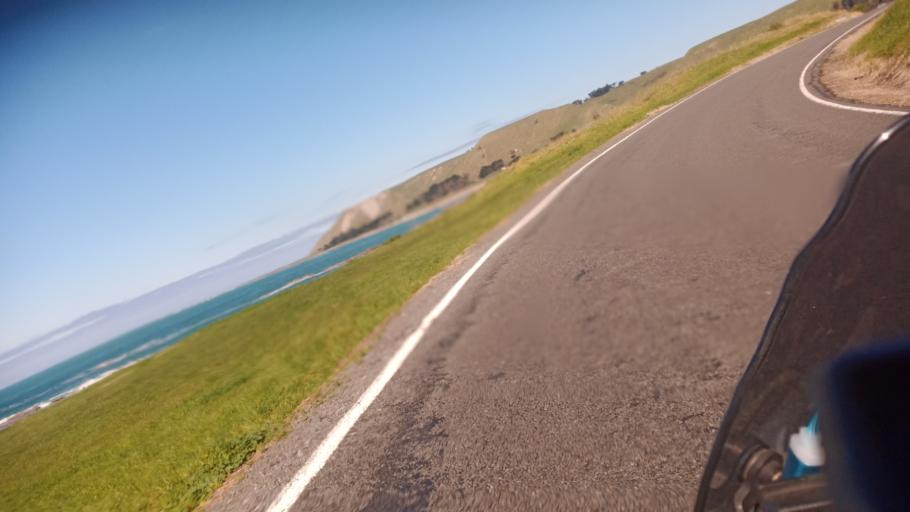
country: NZ
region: Gisborne
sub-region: Gisborne District
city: Gisborne
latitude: -39.0900
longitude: 177.9617
